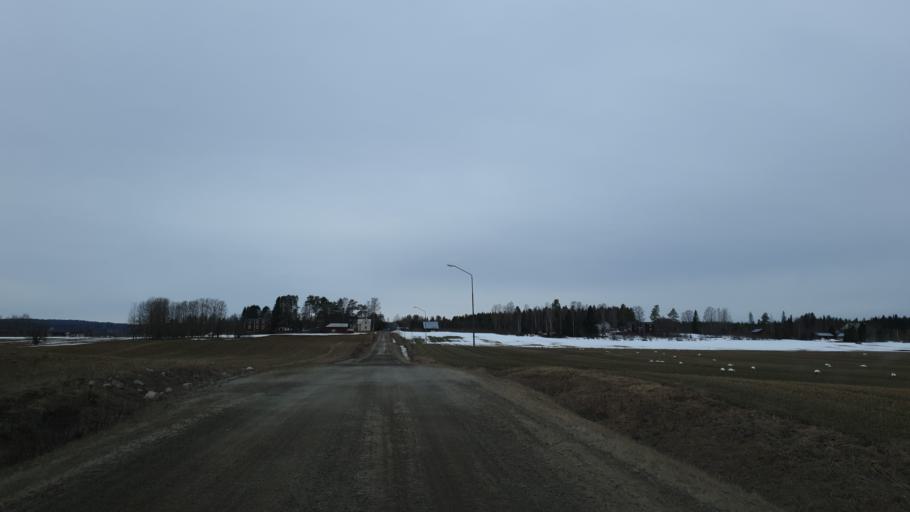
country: SE
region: Vaesterbotten
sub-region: Robertsfors Kommun
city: Robertsfors
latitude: 64.3797
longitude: 20.9122
